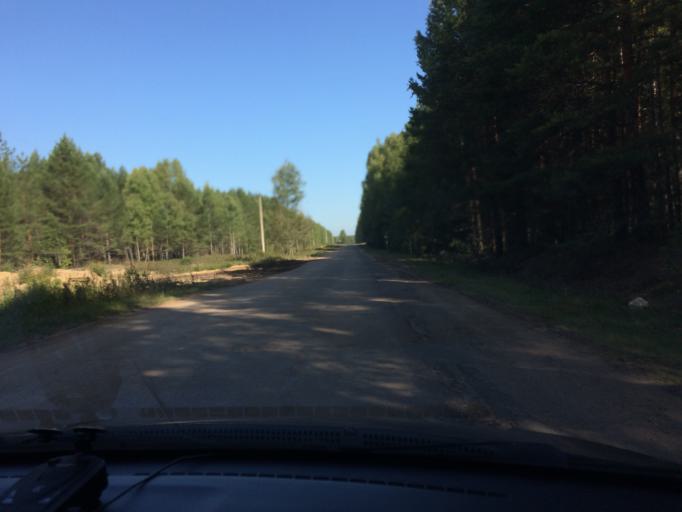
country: RU
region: Mariy-El
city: Sovetskiy
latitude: 56.5725
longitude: 48.4304
